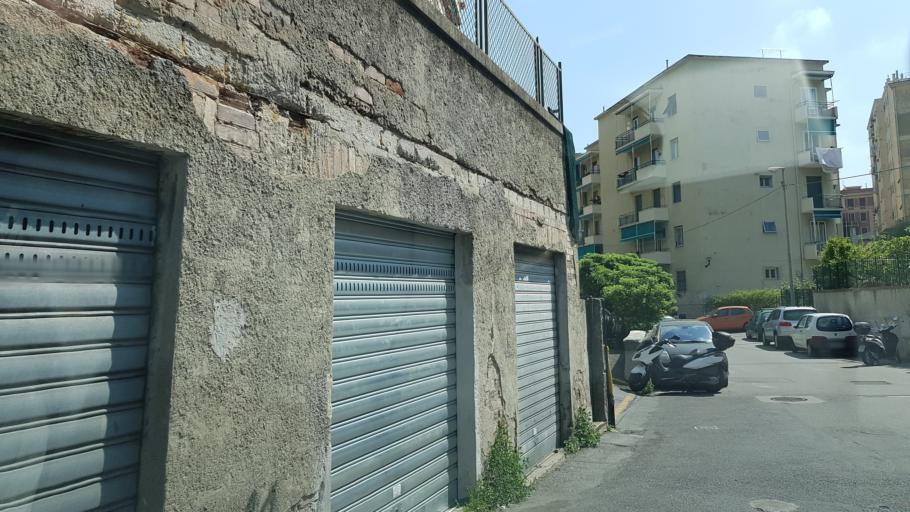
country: IT
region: Liguria
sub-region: Provincia di Genova
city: Genoa
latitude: 44.3964
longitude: 8.9783
